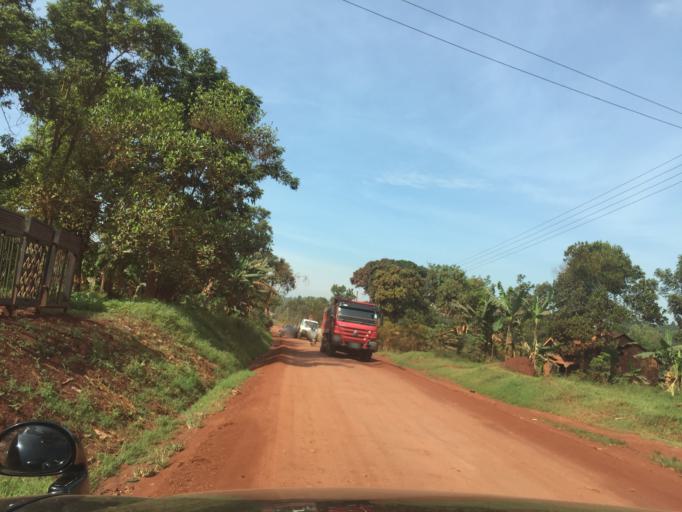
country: UG
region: Central Region
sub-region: Wakiso District
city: Wakiso
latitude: 0.4649
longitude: 32.5360
